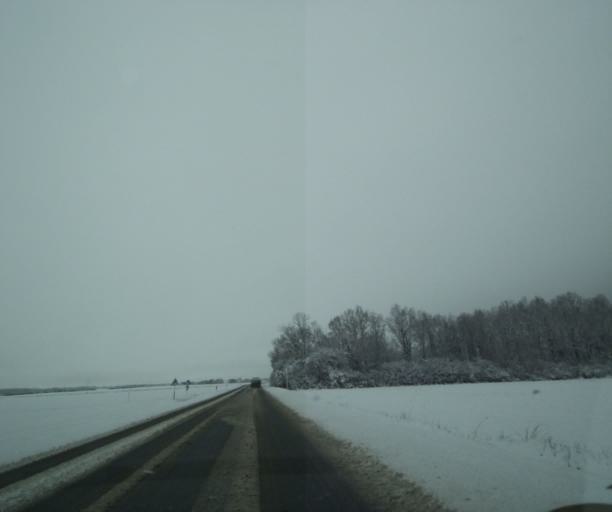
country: FR
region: Champagne-Ardenne
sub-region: Departement de la Haute-Marne
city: Wassy
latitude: 48.5600
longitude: 4.9242
